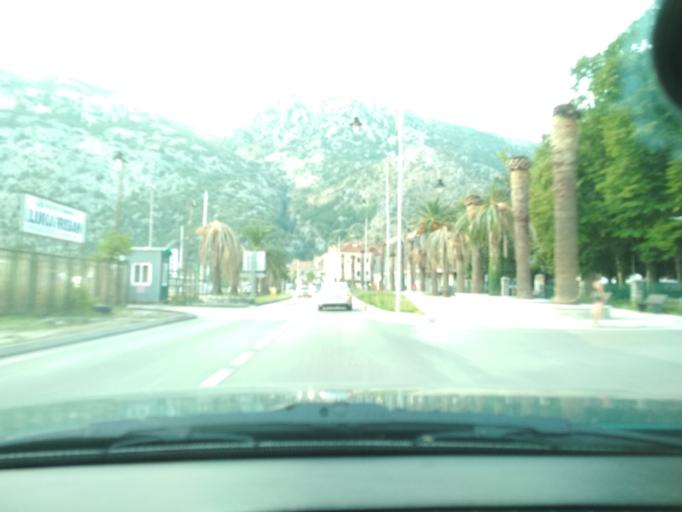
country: ME
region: Kotor
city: Risan
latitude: 42.5135
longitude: 18.6949
